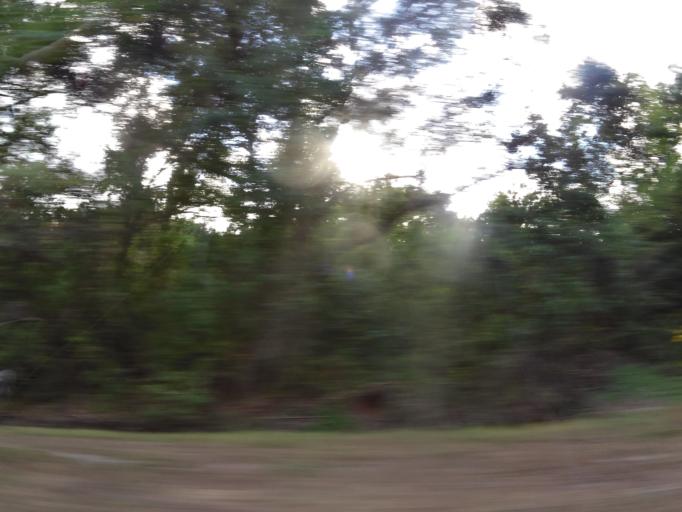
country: US
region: Georgia
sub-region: Liberty County
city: Midway
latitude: 31.6939
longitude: -81.4105
